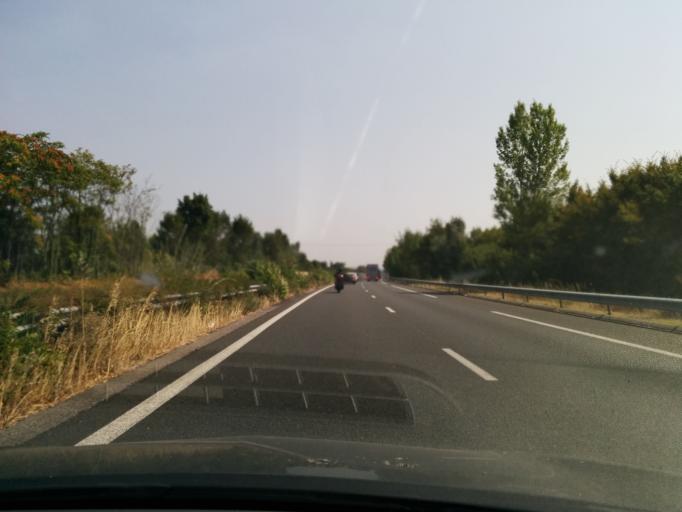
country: FR
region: Midi-Pyrenees
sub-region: Departement du Tarn
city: Marssac-sur-Tarn
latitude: 43.9050
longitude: 2.0383
